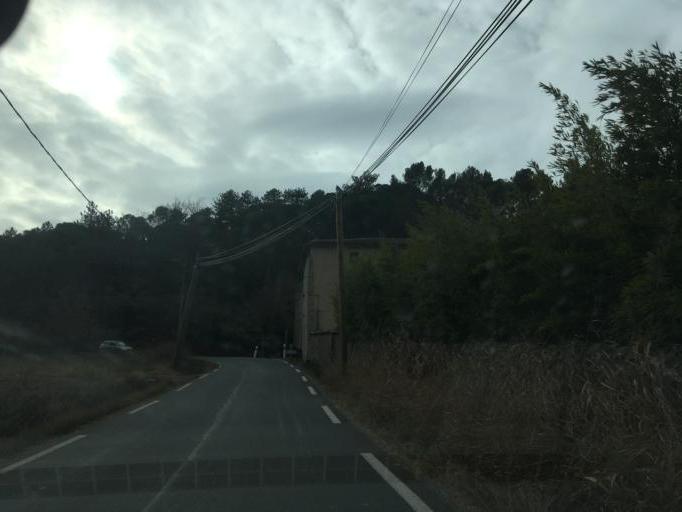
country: FR
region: Provence-Alpes-Cote d'Azur
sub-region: Departement du Var
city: Bras
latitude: 43.4608
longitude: 5.9649
